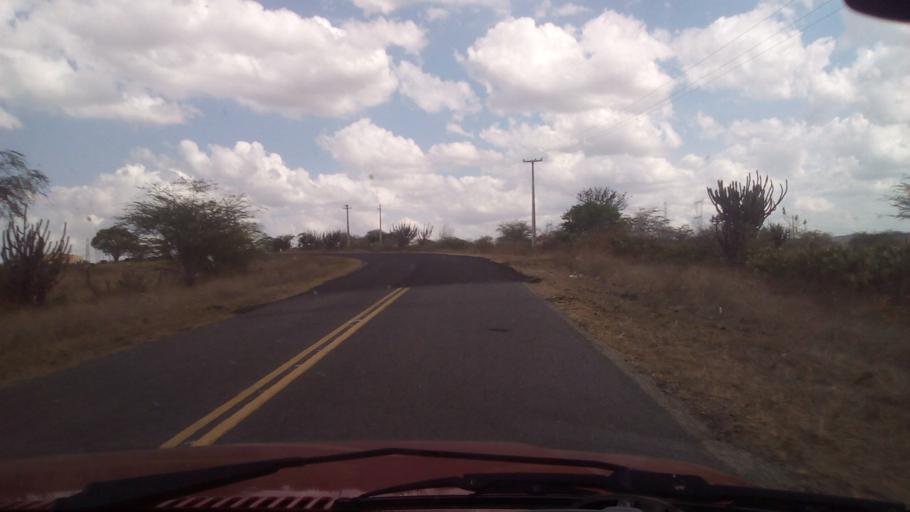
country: BR
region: Paraiba
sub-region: Cacimba De Dentro
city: Cacimba de Dentro
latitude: -6.7012
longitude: -35.7320
